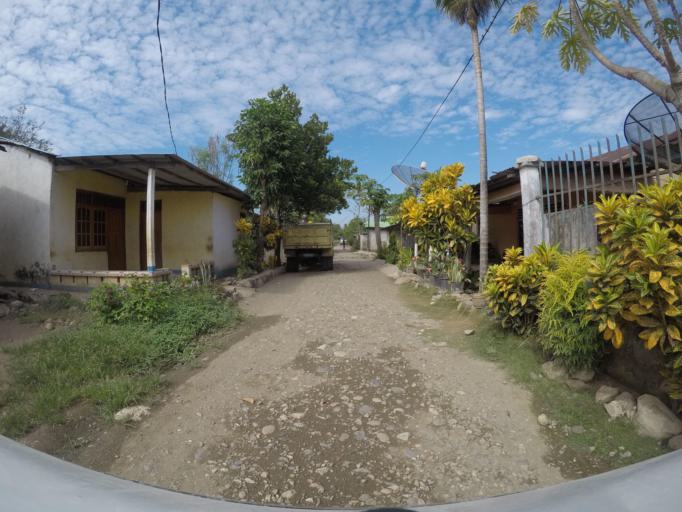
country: TL
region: Bobonaro
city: Maliana
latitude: -8.9825
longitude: 125.2091
